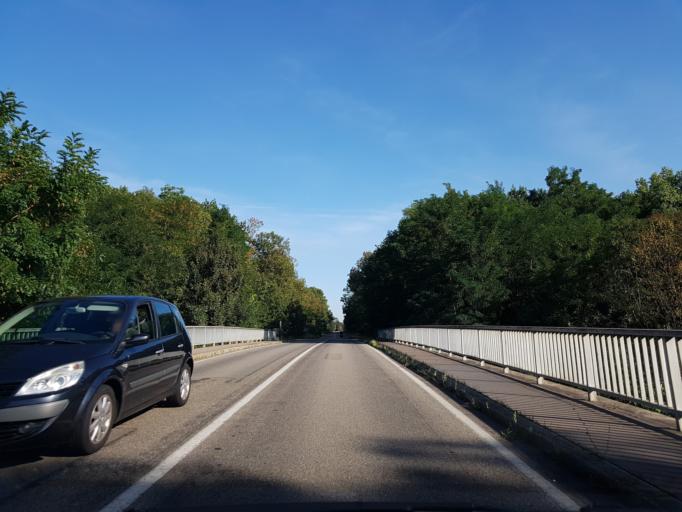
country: FR
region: Alsace
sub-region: Departement du Haut-Rhin
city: Pulversheim
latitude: 47.8431
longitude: 7.2861
